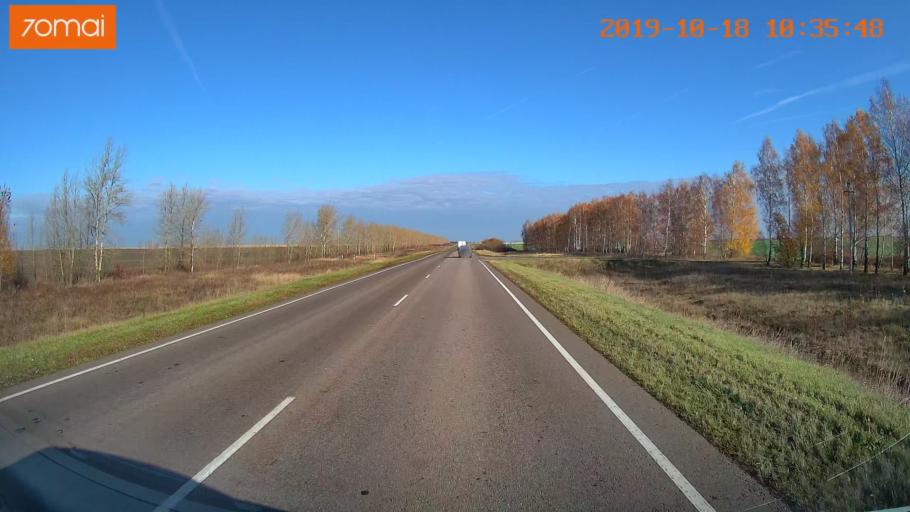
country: RU
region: Tula
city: Kurkino
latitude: 53.5384
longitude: 38.6220
